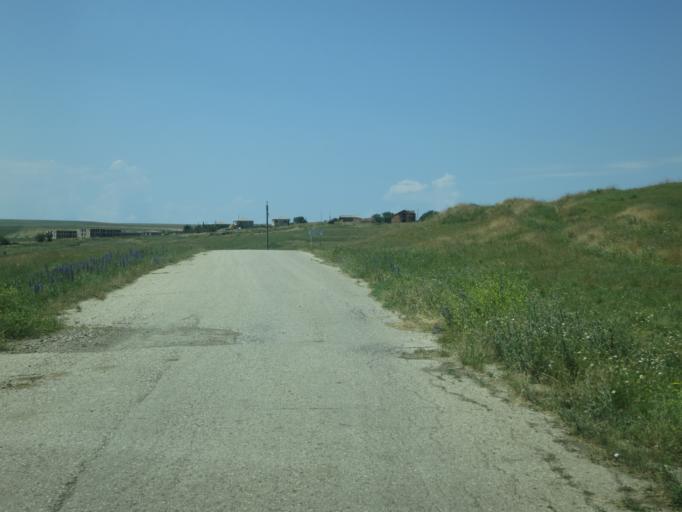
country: GE
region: Kakheti
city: Sagarejo
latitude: 41.5084
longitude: 45.3875
